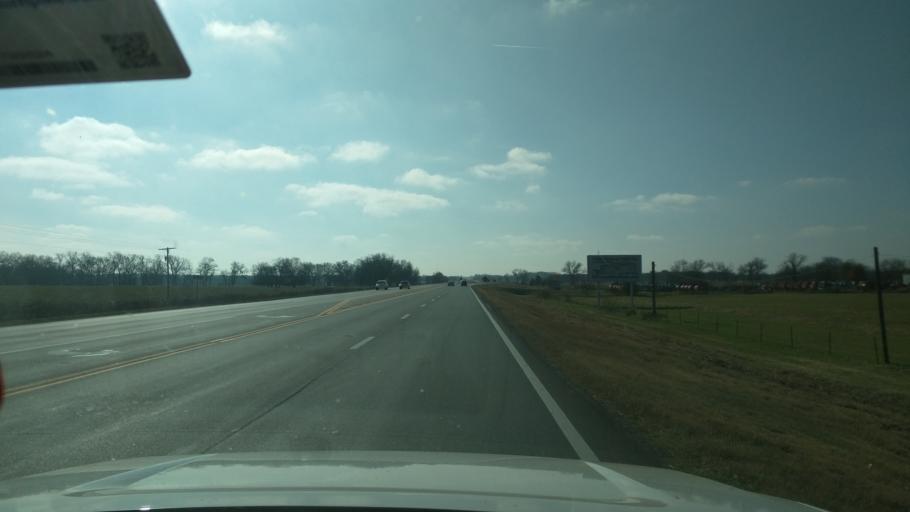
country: US
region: Oklahoma
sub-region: Washington County
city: Bartlesville
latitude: 36.6701
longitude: -95.9353
